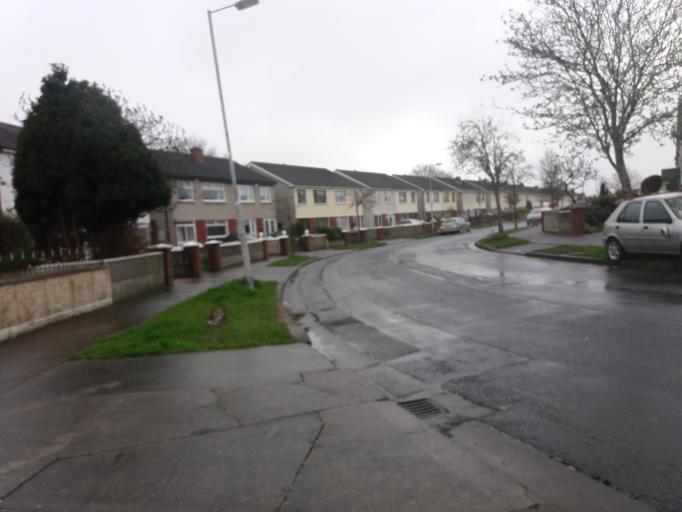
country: IE
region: Leinster
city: Ballymun
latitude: 53.3958
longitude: -6.2782
